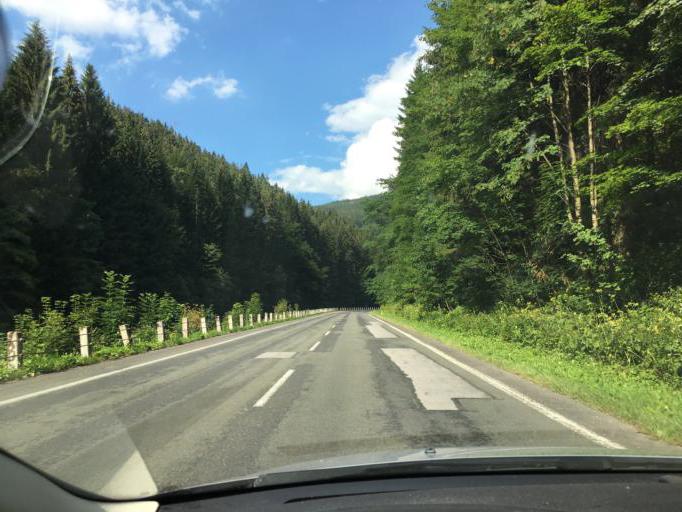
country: CZ
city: Benecko
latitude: 50.6943
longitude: 15.5802
